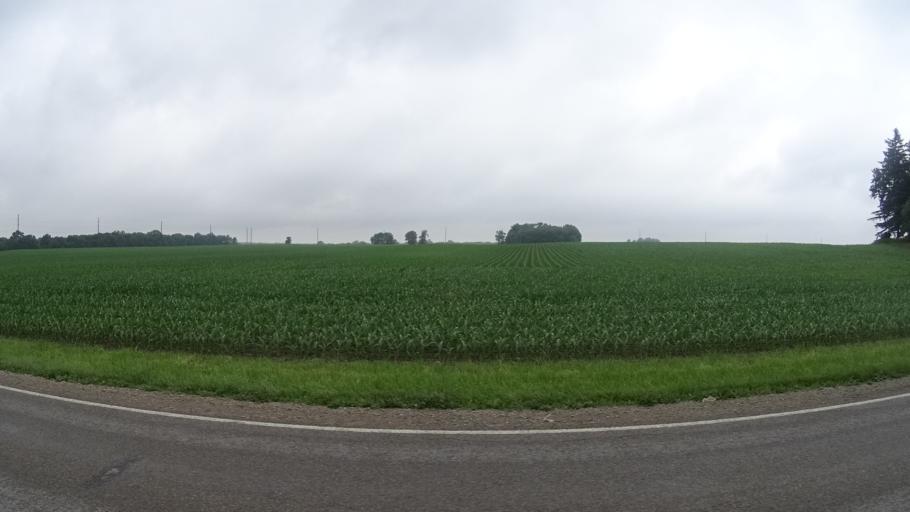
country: US
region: Ohio
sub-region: Huron County
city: Bellevue
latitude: 41.3469
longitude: -82.7643
